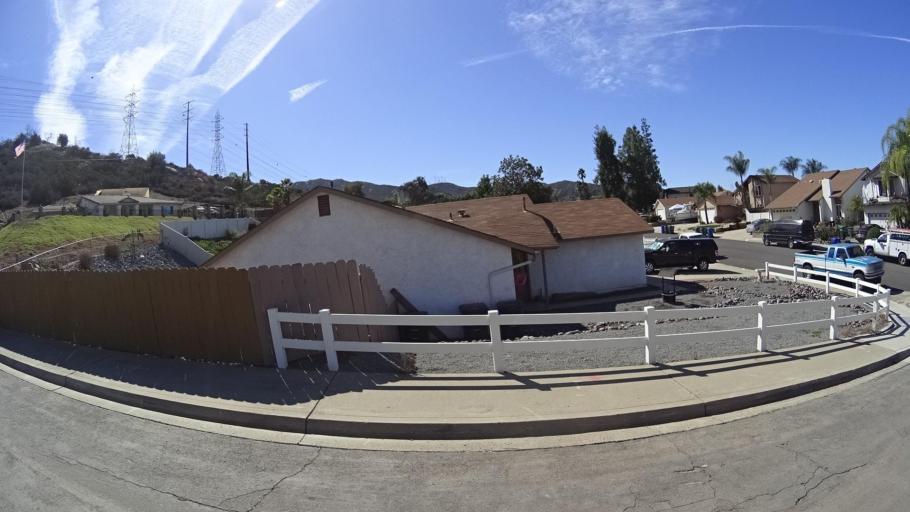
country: US
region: California
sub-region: San Diego County
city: Crest
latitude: 32.8355
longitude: -116.8869
